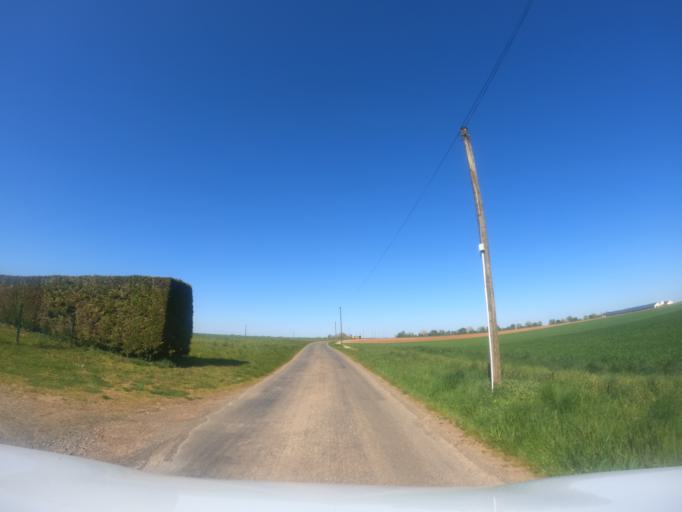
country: FR
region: Pays de la Loire
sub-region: Departement de la Vendee
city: Fontenay-le-Comte
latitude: 46.4179
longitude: -0.7998
